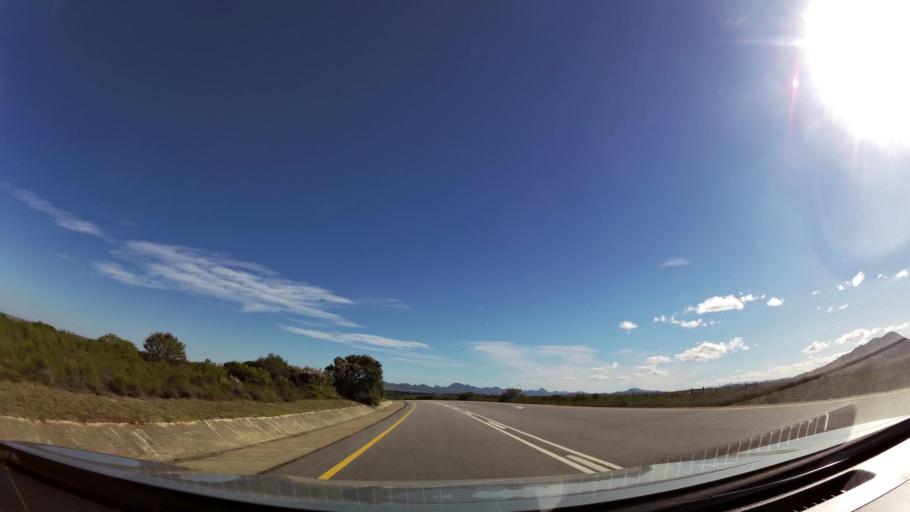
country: ZA
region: Eastern Cape
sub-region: Cacadu District Municipality
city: Kruisfontein
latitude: -34.0101
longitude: 24.6524
